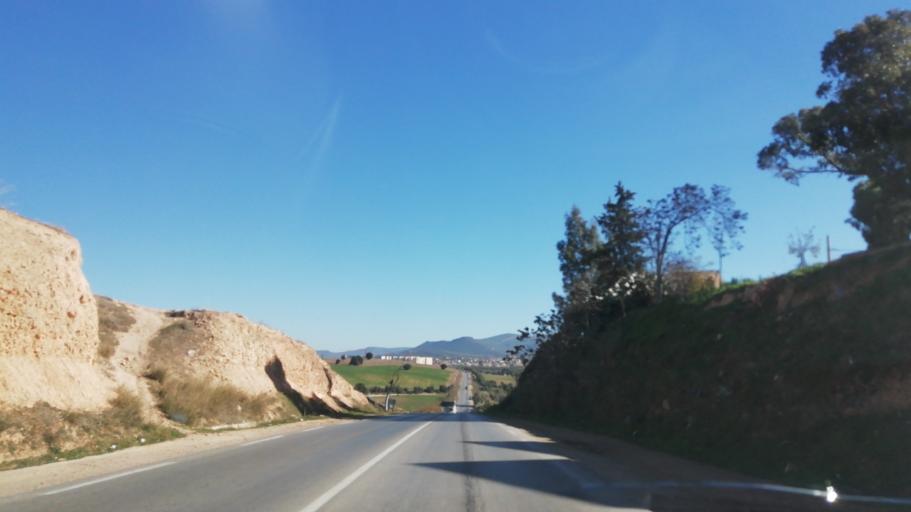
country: DZ
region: Tlemcen
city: Beni Mester
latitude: 34.8249
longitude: -1.5539
